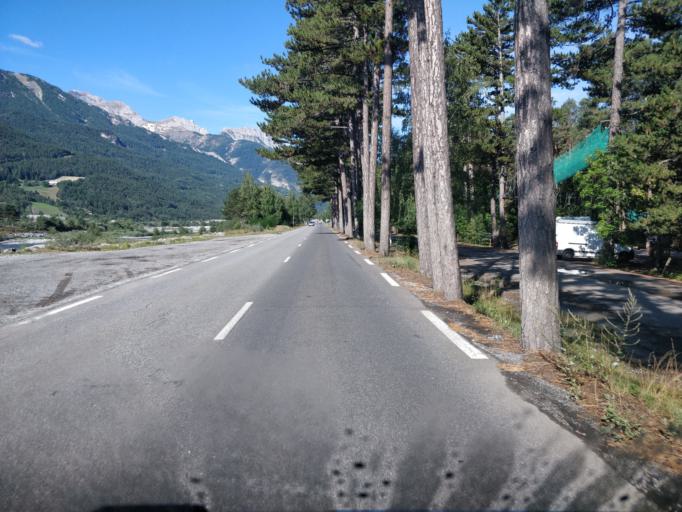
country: FR
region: Provence-Alpes-Cote d'Azur
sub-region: Departement des Alpes-de-Haute-Provence
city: Barcelonnette
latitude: 44.3863
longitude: 6.6259
